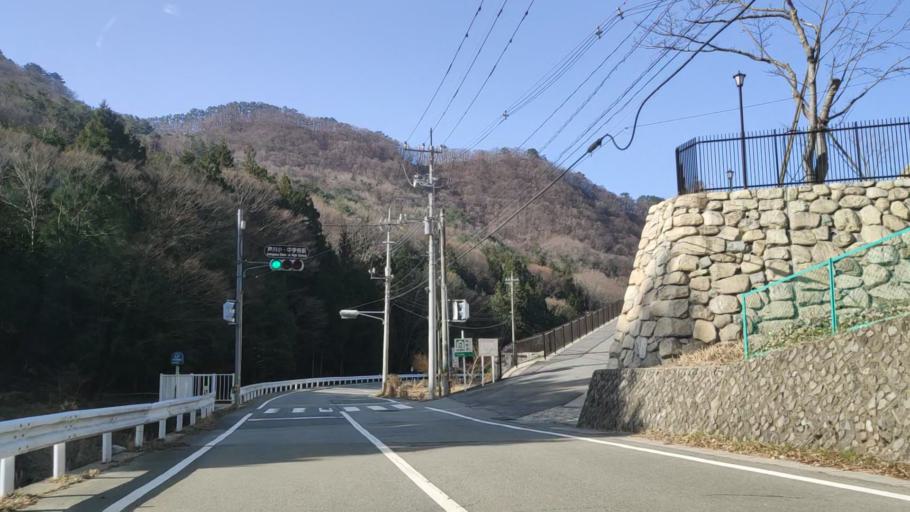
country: JP
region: Yamanashi
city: Fujikawaguchiko
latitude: 35.5552
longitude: 138.6716
